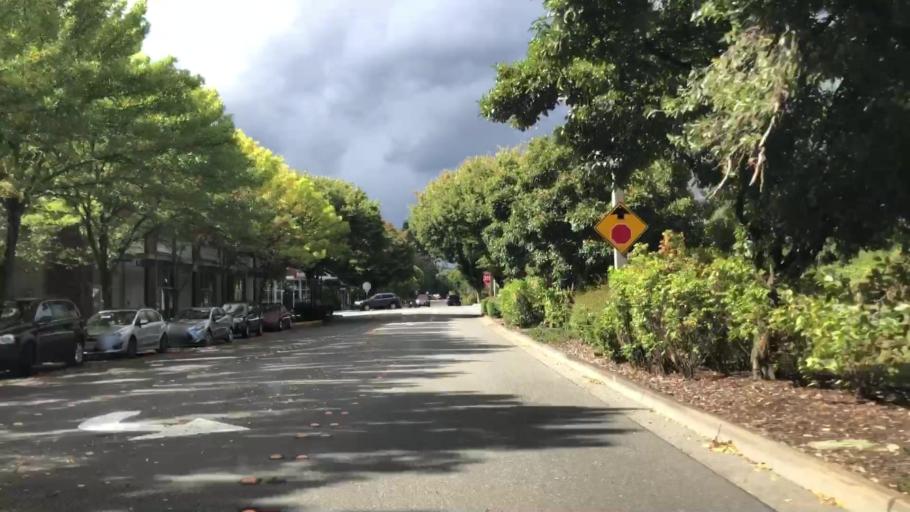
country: US
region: Washington
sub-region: King County
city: Redmond
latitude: 47.6713
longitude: -122.1178
